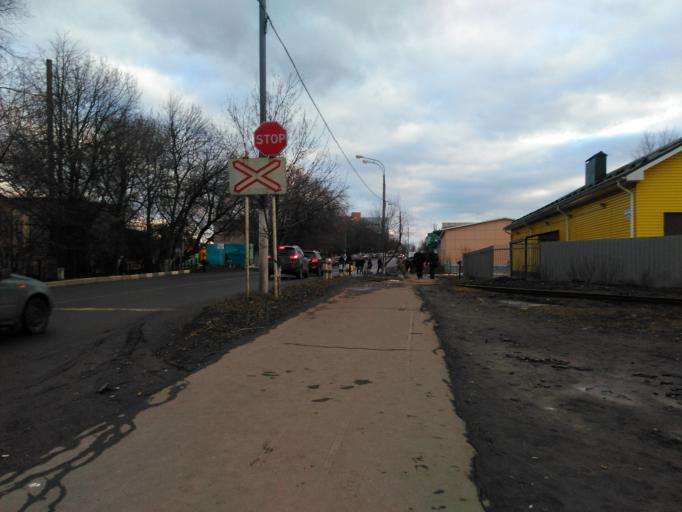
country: RU
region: Moscow
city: Nagornyy
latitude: 55.6551
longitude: 37.6238
